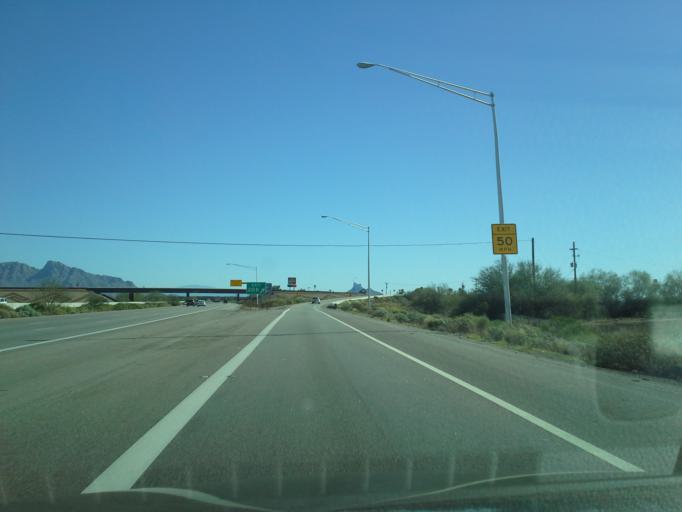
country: US
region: Arizona
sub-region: Pinal County
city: Eloy
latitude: 32.7364
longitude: -111.5537
